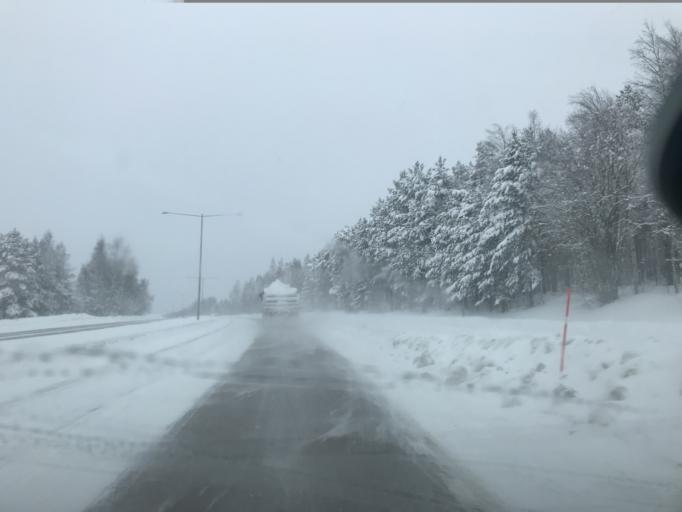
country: SE
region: Norrbotten
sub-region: Lulea Kommun
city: Lulea
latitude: 65.6065
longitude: 22.1384
